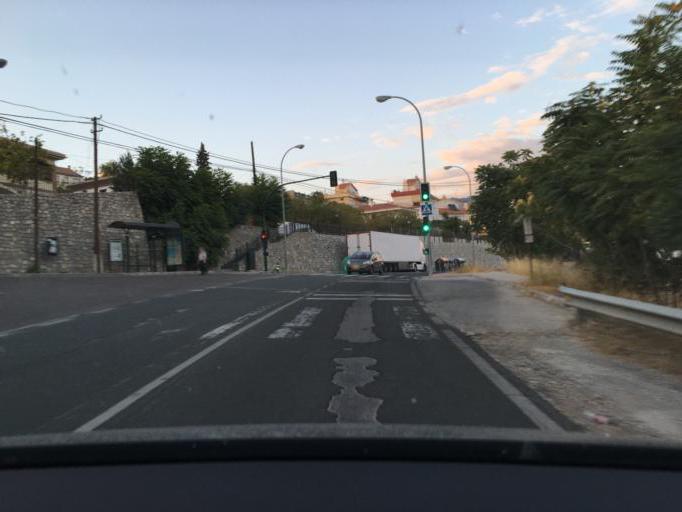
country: ES
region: Andalusia
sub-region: Provincia de Granada
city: Viznar
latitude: 37.2091
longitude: -3.5568
